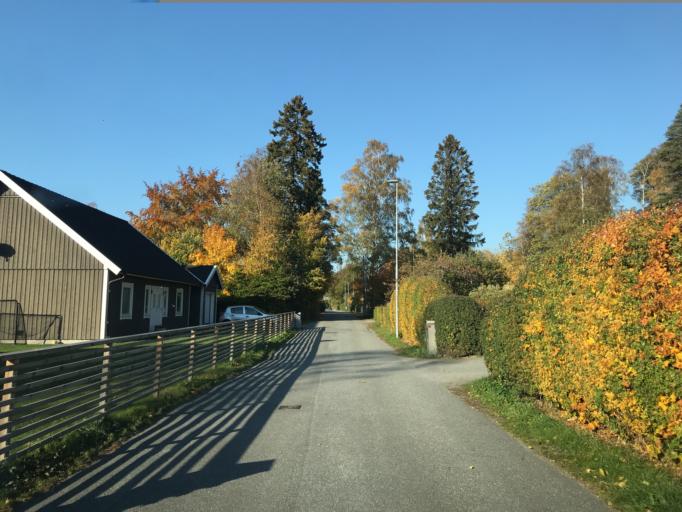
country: SE
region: Stockholm
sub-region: Sollentuna Kommun
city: Sollentuna
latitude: 59.4228
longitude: 17.9348
